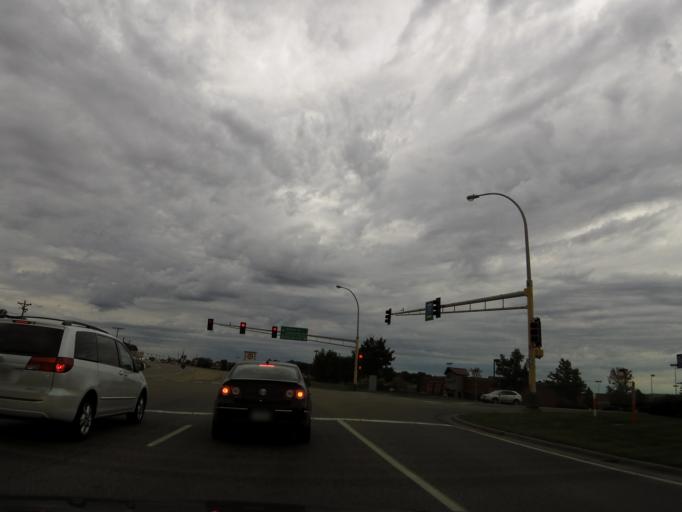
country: US
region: Minnesota
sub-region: Scott County
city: Prior Lake
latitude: 44.7418
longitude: -93.3801
